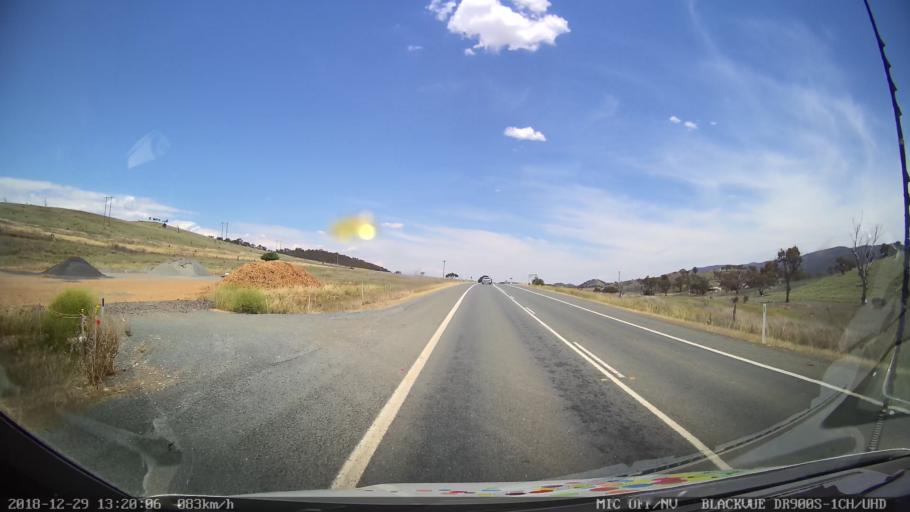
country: AU
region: Australian Capital Territory
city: Macarthur
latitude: -35.7746
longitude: 149.1620
